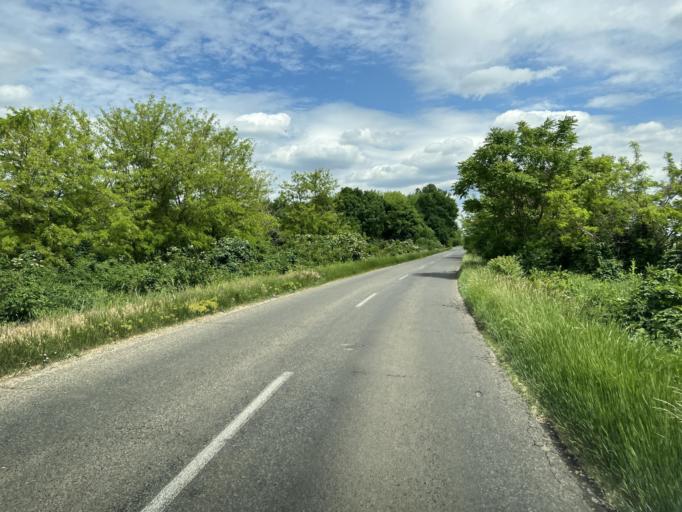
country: HU
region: Pest
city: Toalmas
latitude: 47.4850
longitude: 19.6383
